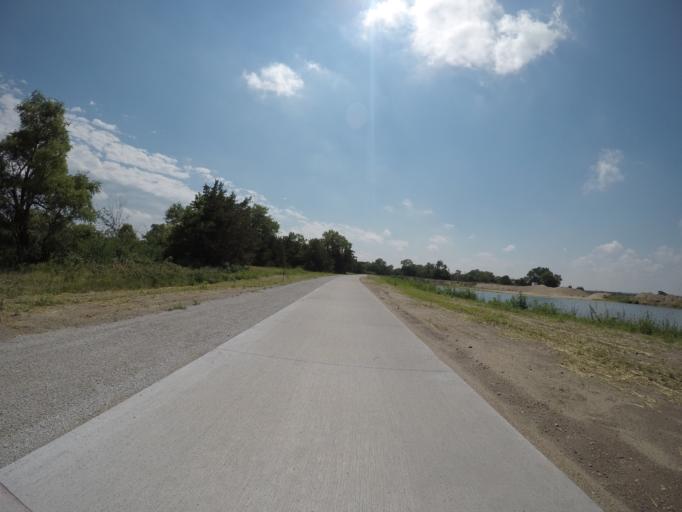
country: US
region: Nebraska
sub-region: Buffalo County
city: Kearney
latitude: 40.6738
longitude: -99.0153
